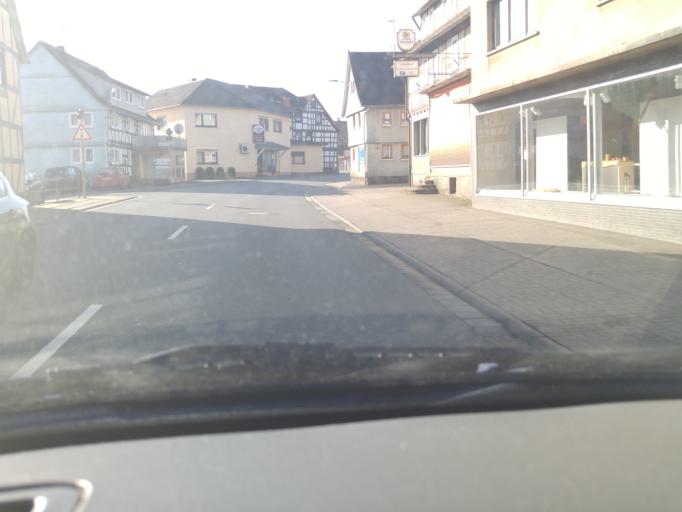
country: DE
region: Hesse
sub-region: Regierungsbezirk Giessen
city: Lauterbach
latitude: 50.6283
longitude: 9.4447
